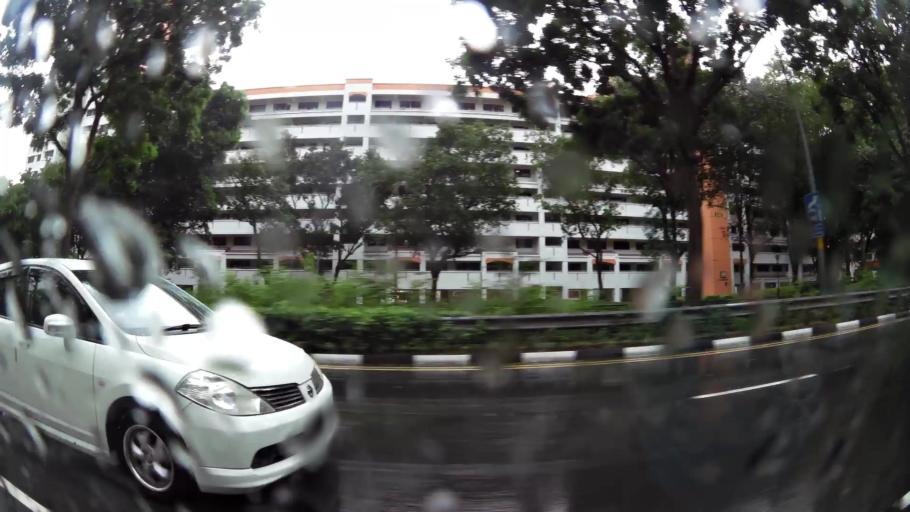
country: MY
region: Johor
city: Kampung Pasir Gudang Baru
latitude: 1.3800
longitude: 103.8915
